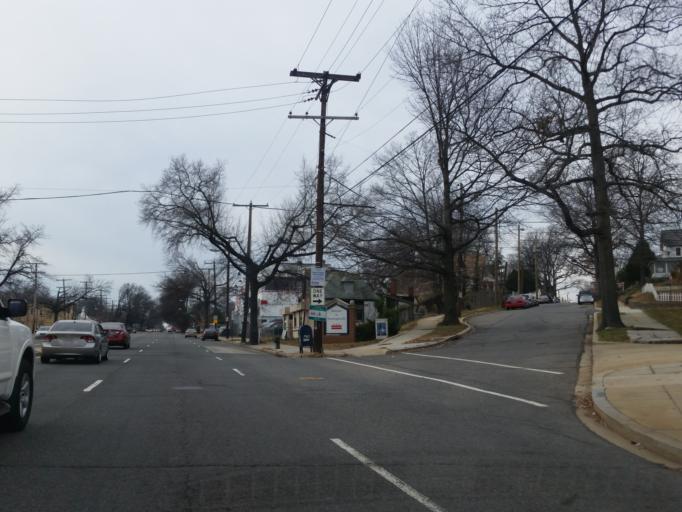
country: US
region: Maryland
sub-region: Prince George's County
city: Mount Rainier
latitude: 38.9351
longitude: -76.9638
